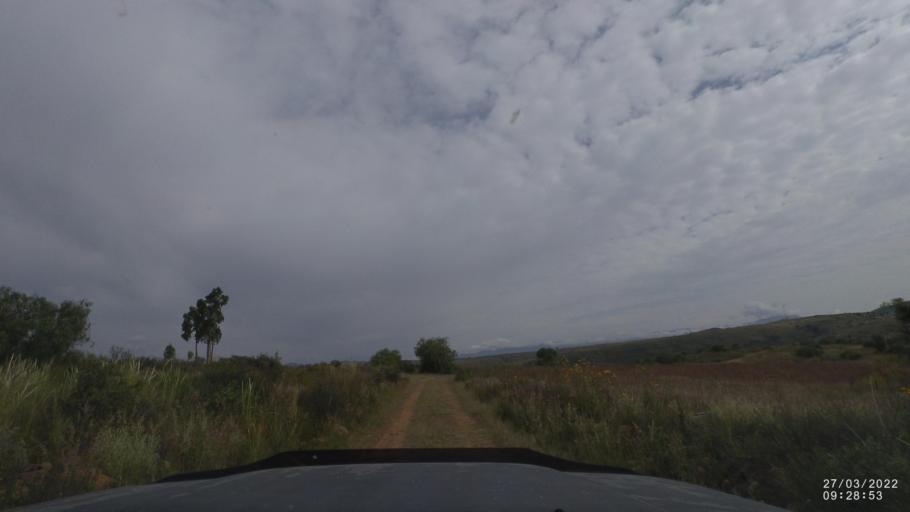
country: BO
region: Cochabamba
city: Cliza
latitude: -17.7285
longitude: -65.8793
